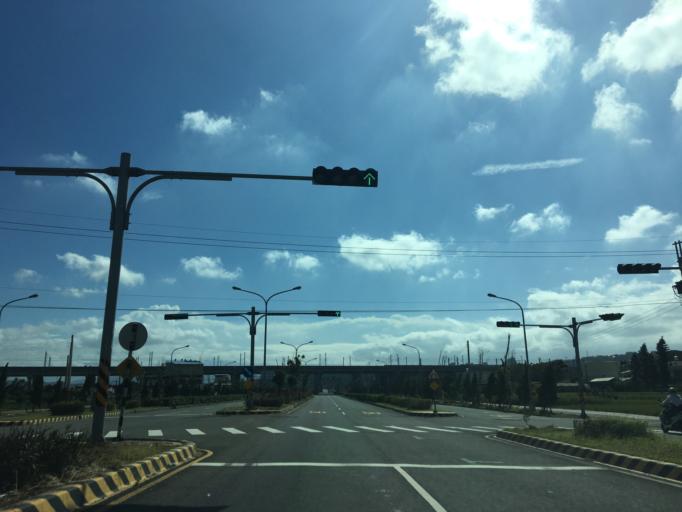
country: TW
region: Taiwan
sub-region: Hsinchu
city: Zhubei
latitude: 24.7874
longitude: 121.0311
